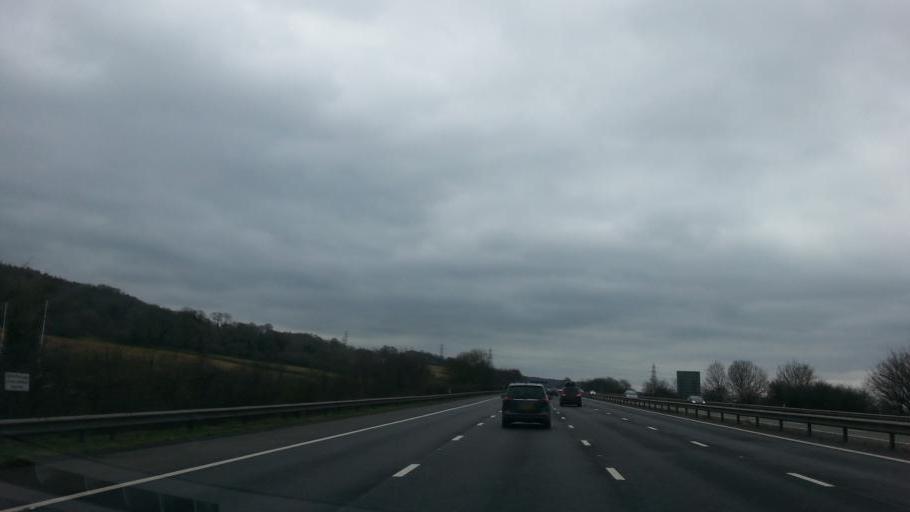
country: GB
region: England
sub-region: North Somerset
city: Easton-in-Gordano
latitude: 51.4730
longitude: -2.7324
